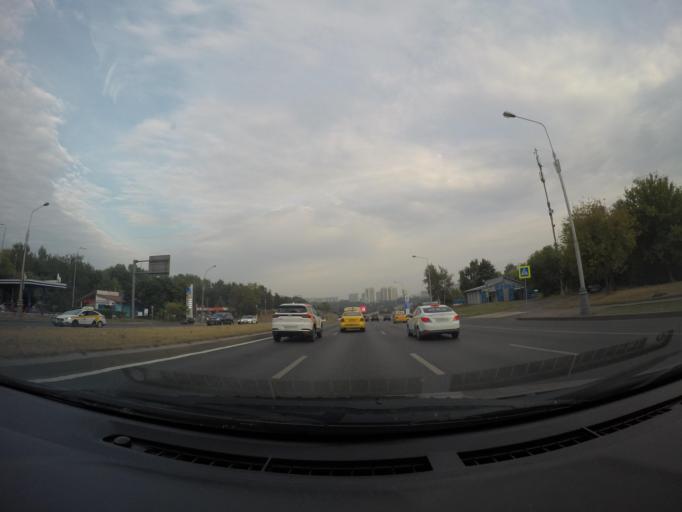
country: RU
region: Moskovskaya
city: Kur'yanovo
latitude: 55.6340
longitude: 37.7006
